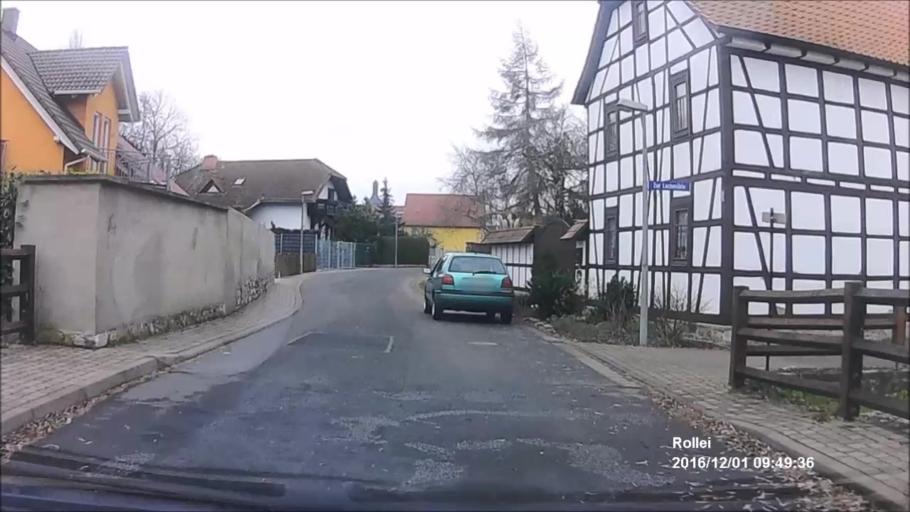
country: DE
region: Thuringia
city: Elxleben
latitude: 51.0372
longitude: 10.9714
